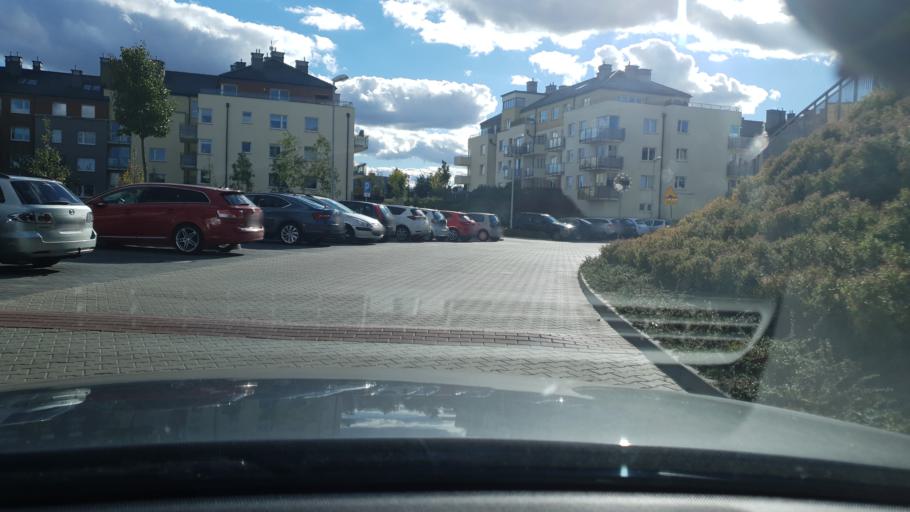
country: PL
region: Pomeranian Voivodeship
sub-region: Gdynia
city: Wielki Kack
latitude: 54.4936
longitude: 18.4413
